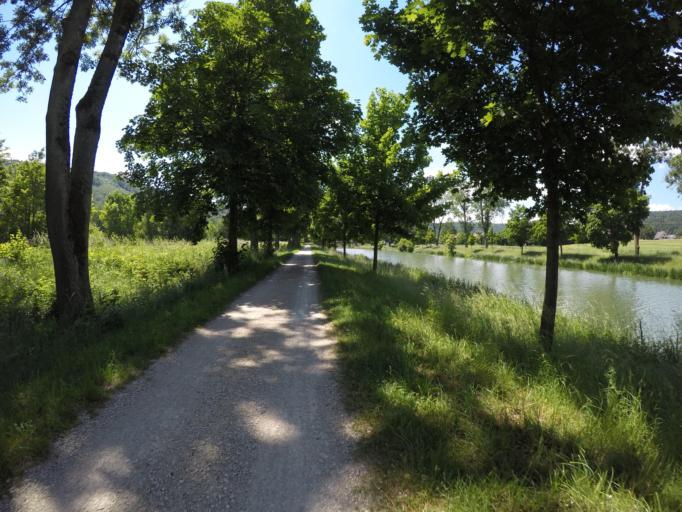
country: DE
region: Bavaria
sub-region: Lower Bavaria
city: Essing
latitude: 48.9254
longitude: 11.8084
